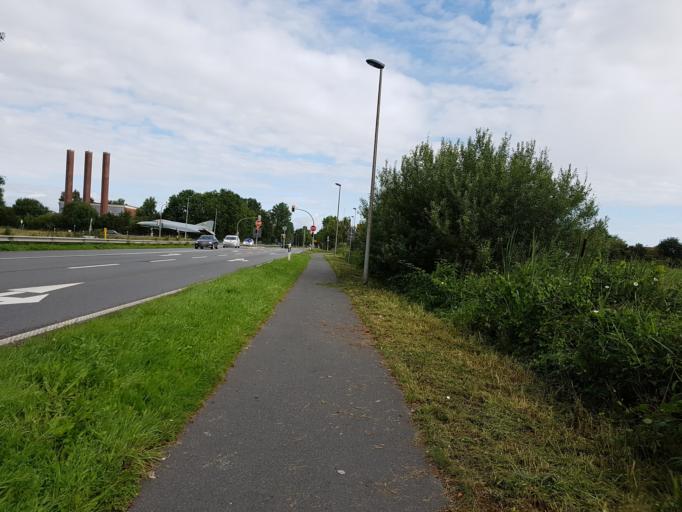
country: DE
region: Lower Saxony
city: Wittmund
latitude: 53.5669
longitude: 7.7837
